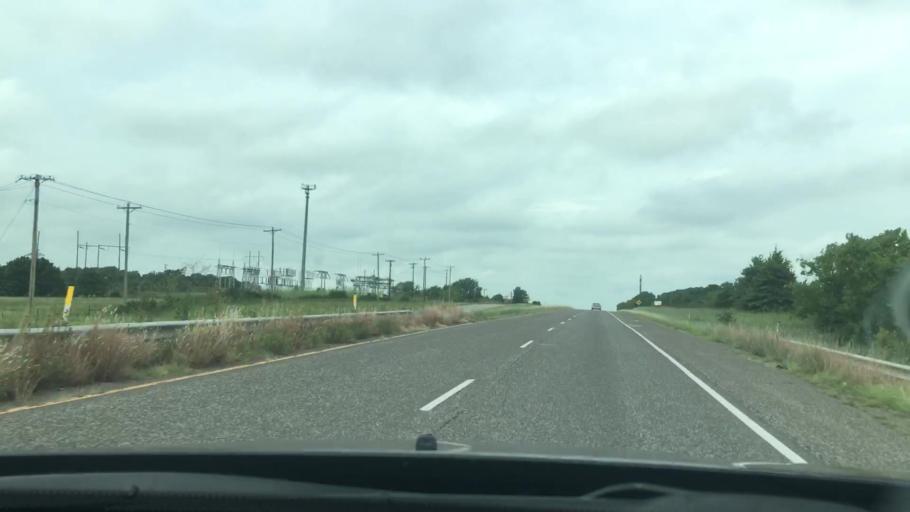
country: US
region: Oklahoma
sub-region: Carter County
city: Lone Grove
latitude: 34.1730
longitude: -97.3294
